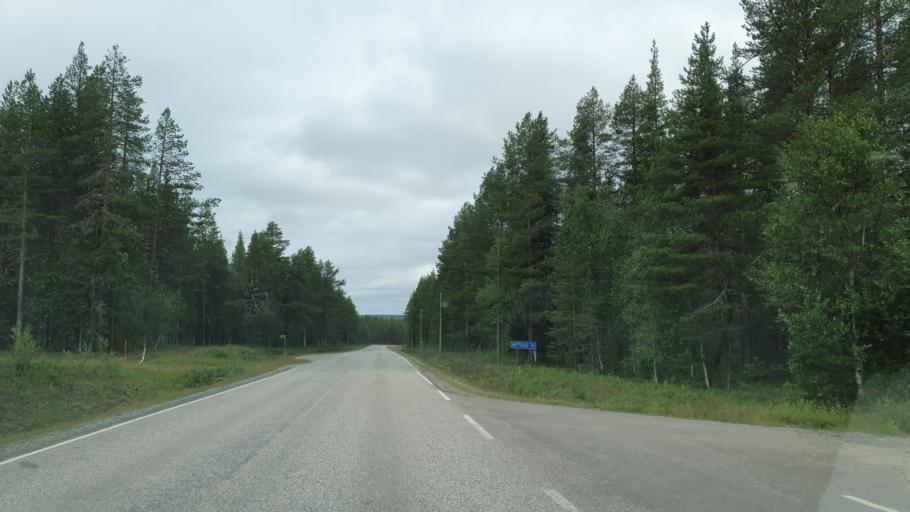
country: FI
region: Lapland
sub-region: Pohjois-Lappi
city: Sodankylae
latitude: 67.4162
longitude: 26.2608
